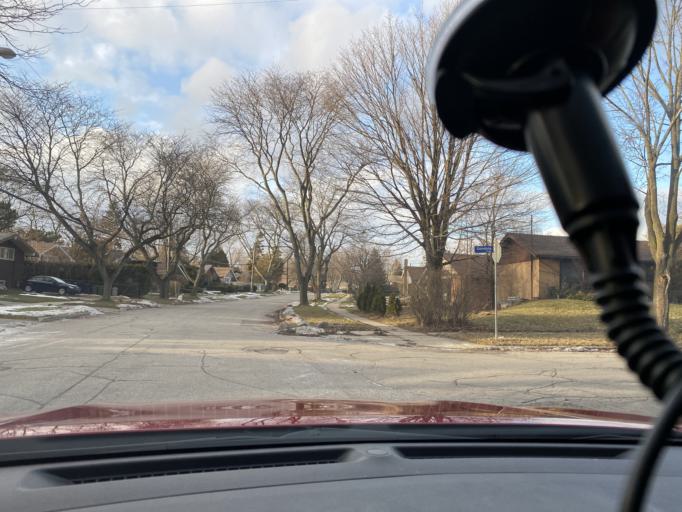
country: CA
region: Ontario
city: Scarborough
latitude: 43.7663
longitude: -79.2095
